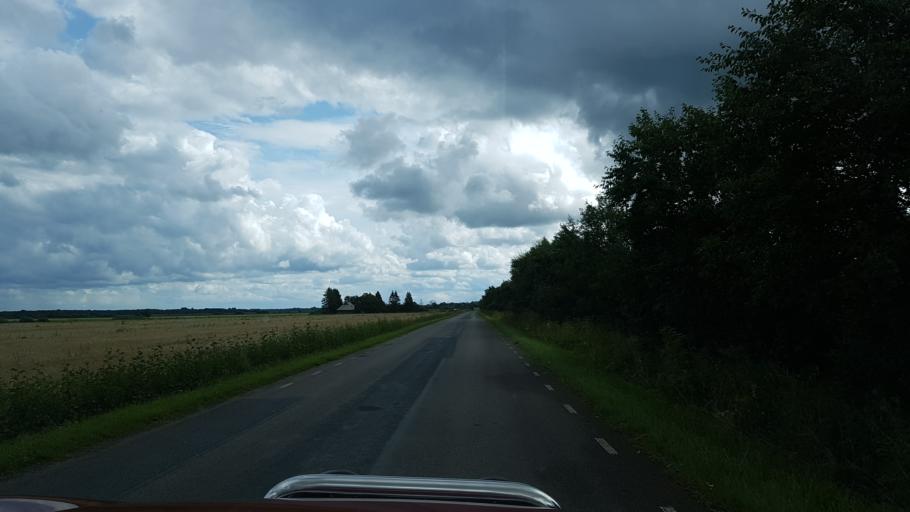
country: EE
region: Laeaene
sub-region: Lihula vald
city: Lihula
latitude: 58.7201
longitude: 23.9772
